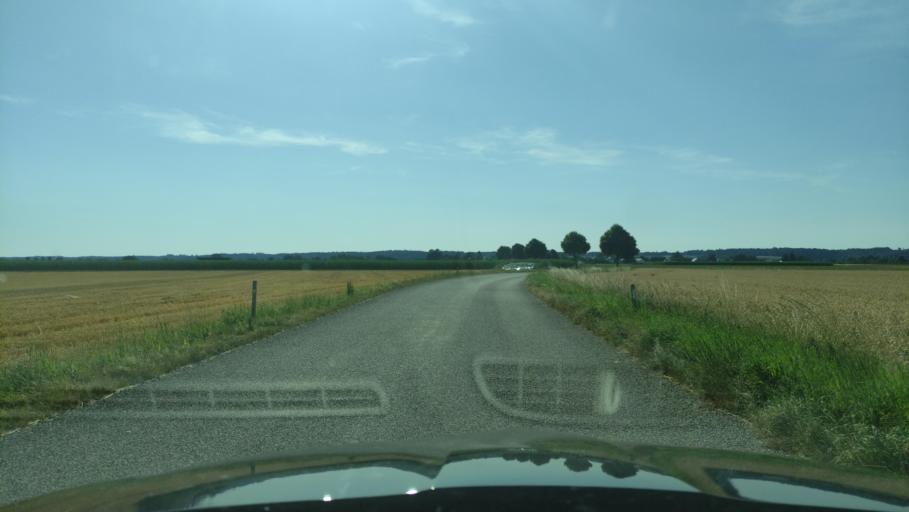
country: DE
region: Bavaria
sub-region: Swabia
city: Ebershausen
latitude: 48.2081
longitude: 10.2999
